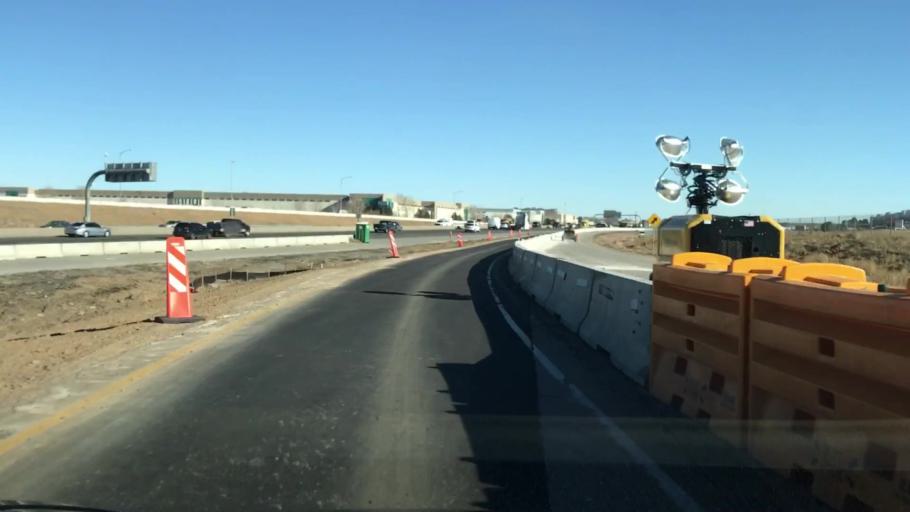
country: US
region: Colorado
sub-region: Adams County
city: Commerce City
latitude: 39.7763
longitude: -104.8794
